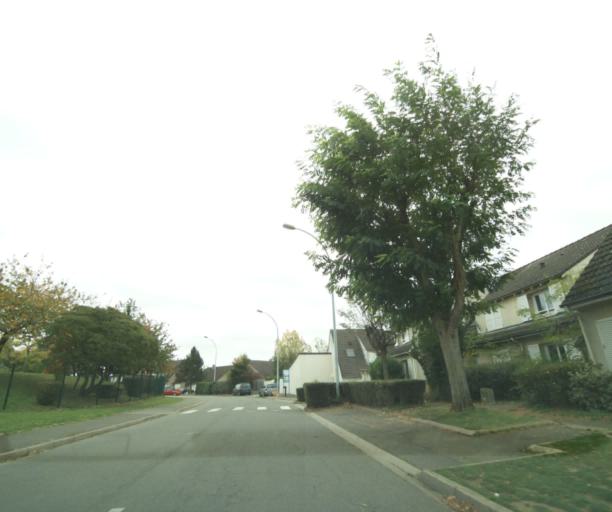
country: FR
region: Centre
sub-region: Departement d'Eure-et-Loir
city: Dreux
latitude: 48.7351
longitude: 1.3488
